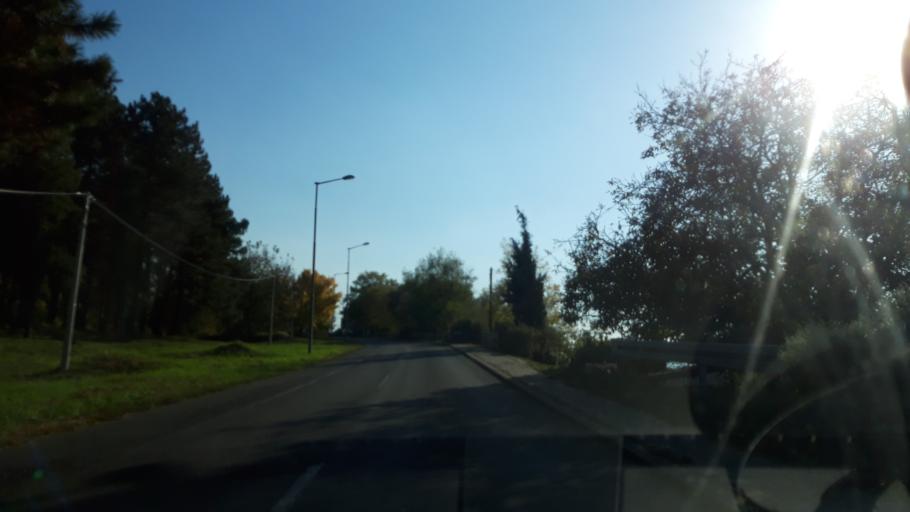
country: RS
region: Autonomna Pokrajina Vojvodina
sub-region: Juznobacki Okrug
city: Petrovaradin
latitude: 45.2430
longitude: 19.8665
